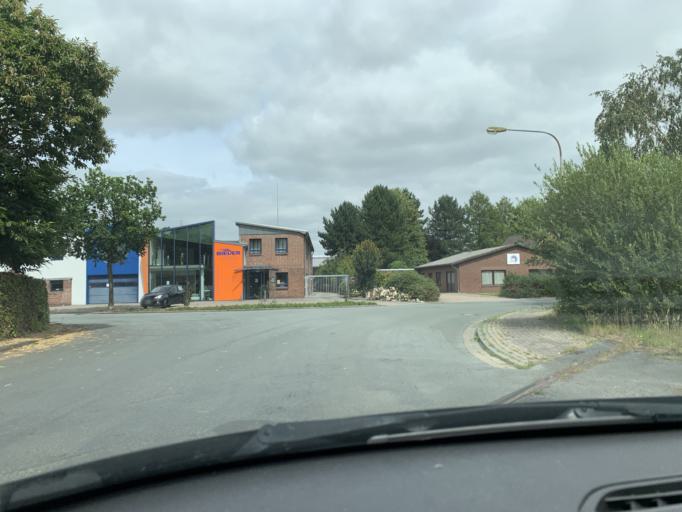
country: DE
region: Lower Saxony
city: Westerstede
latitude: 53.2683
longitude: 7.9457
